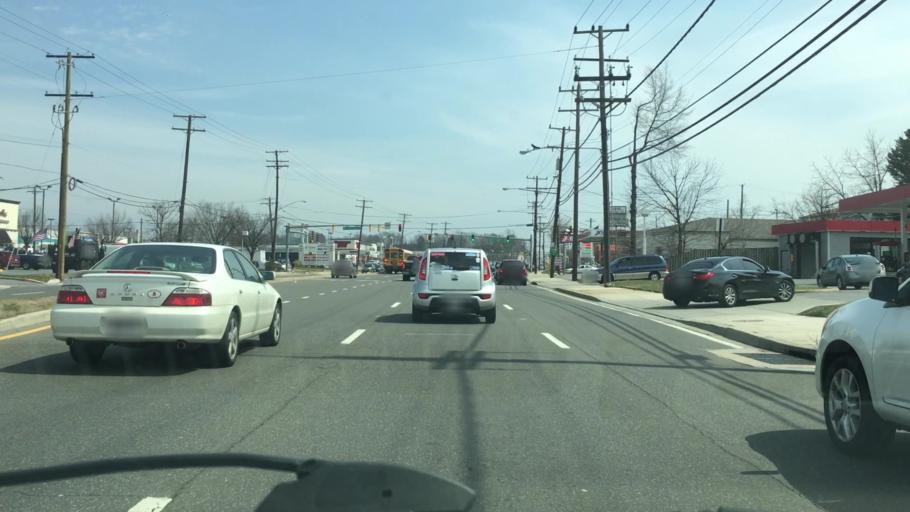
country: US
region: Maryland
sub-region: Prince George's County
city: Berwyn Heights
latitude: 38.9980
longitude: -76.9136
